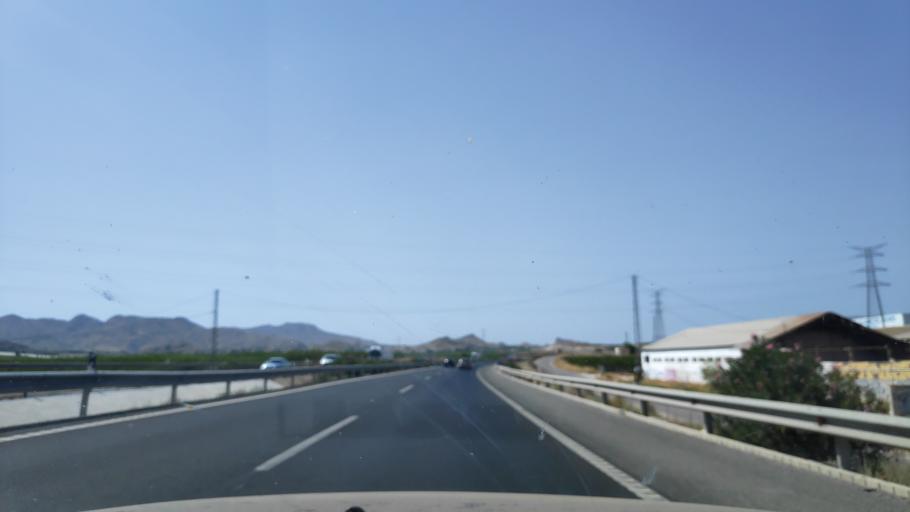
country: ES
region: Murcia
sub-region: Murcia
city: Archena
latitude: 38.1354
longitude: -1.2698
